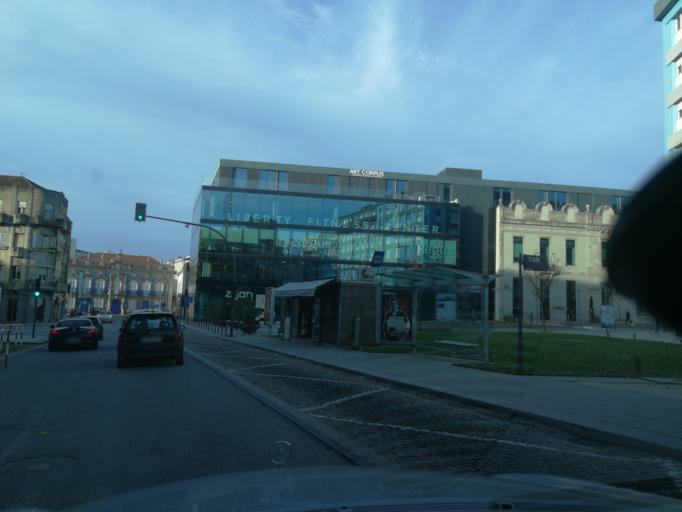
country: PT
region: Braga
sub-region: Braga
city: Braga
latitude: 41.5493
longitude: -8.4212
